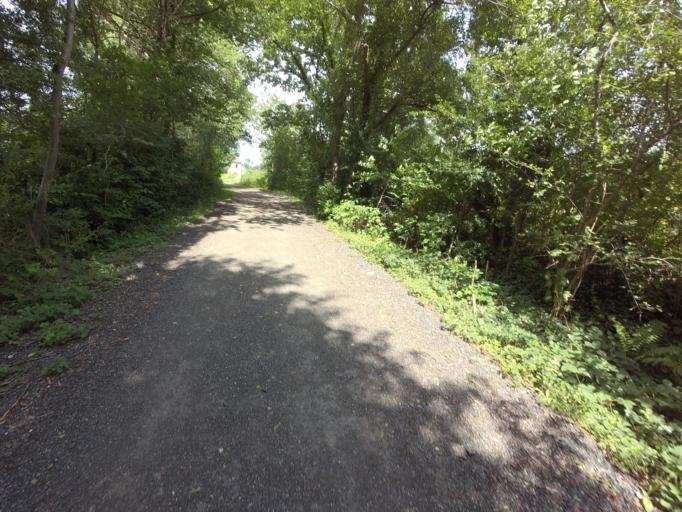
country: BE
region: Wallonia
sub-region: Province de Liege
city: La Calamine
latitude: 50.7180
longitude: 5.9826
